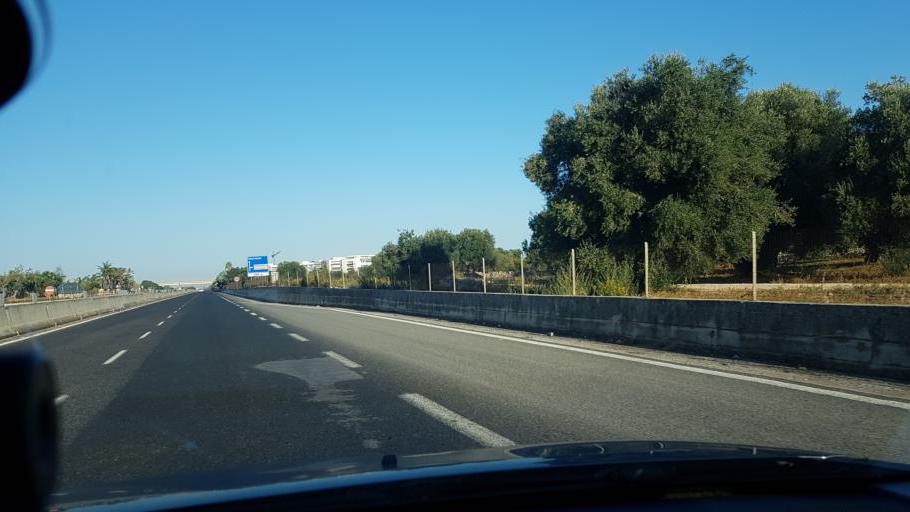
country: IT
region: Apulia
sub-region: Provincia di Bari
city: Monopoli
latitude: 40.9280
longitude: 17.3071
